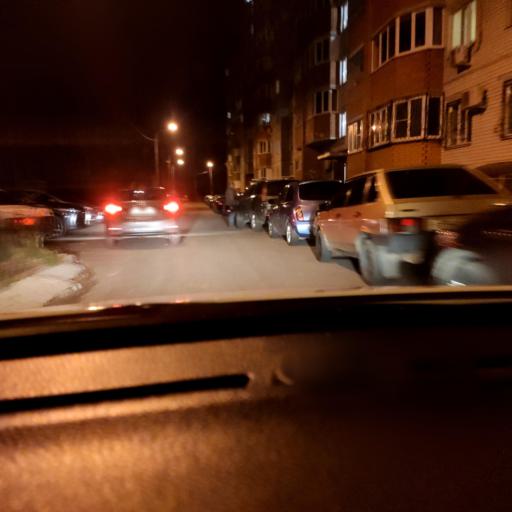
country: RU
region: Voronezj
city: Voronezh
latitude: 51.6932
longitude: 39.2792
